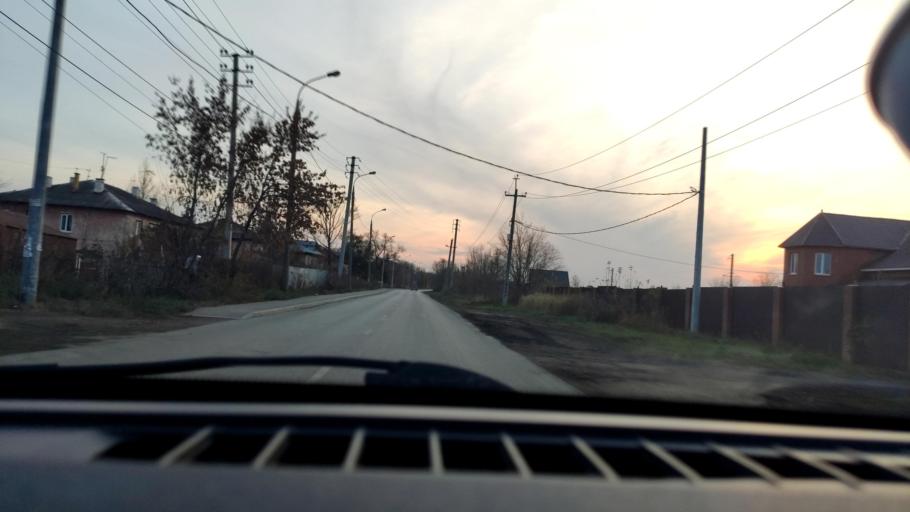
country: RU
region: Samara
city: Samara
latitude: 53.1415
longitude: 50.1315
